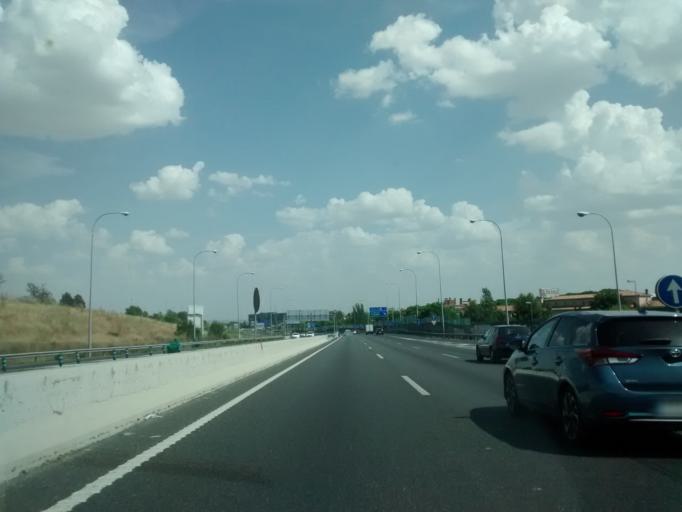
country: ES
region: Madrid
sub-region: Provincia de Madrid
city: San Blas
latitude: 40.4568
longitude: -3.6150
